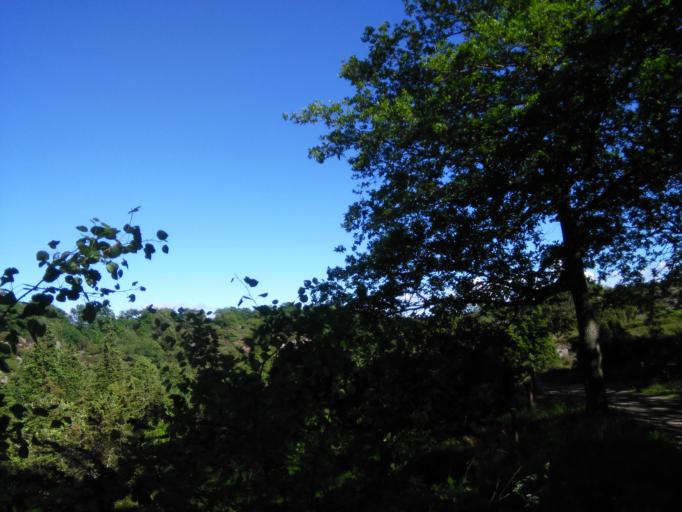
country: DK
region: Capital Region
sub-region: Bornholm Kommune
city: Ronne
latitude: 55.2604
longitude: 14.7670
